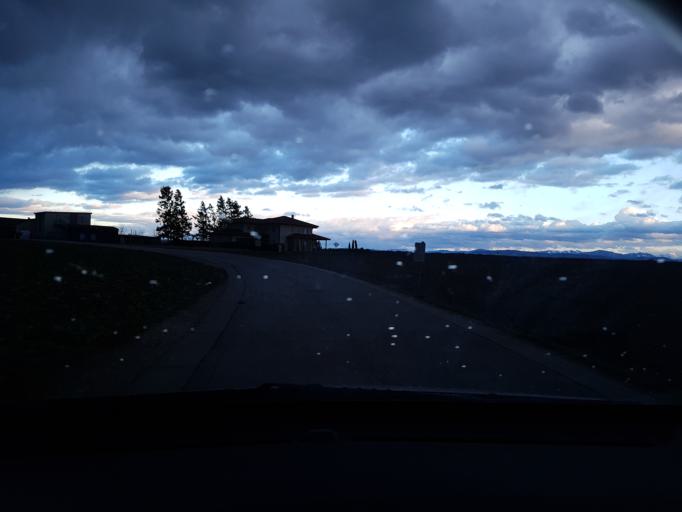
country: AT
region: Upper Austria
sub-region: Politischer Bezirk Linz-Land
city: Ansfelden
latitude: 48.1483
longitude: 14.3157
